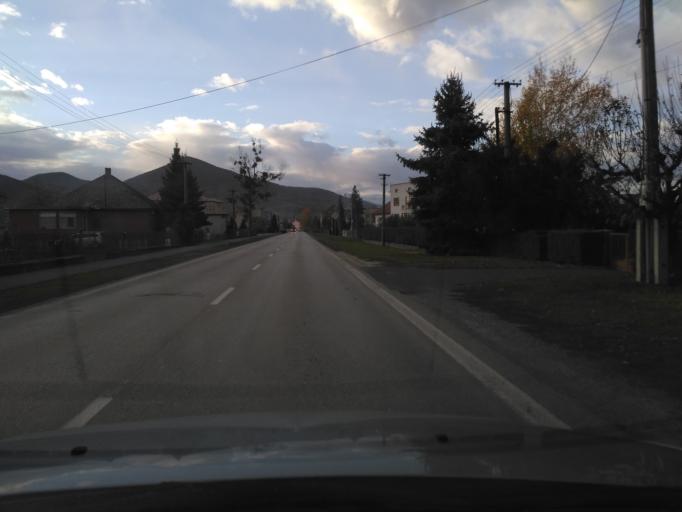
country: HU
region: Borsod-Abauj-Zemplen
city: Satoraljaujhely
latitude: 48.3986
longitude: 21.6789
